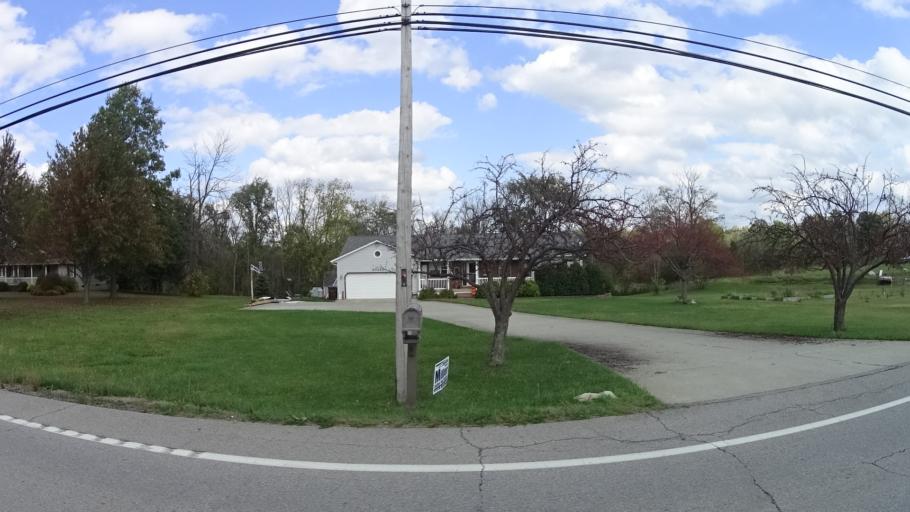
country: US
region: Ohio
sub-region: Lorain County
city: Grafton
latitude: 41.2631
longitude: -82.0430
